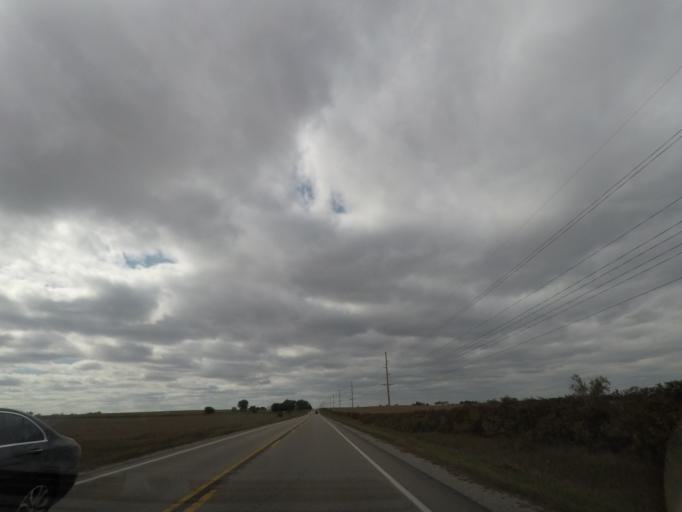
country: US
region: Iowa
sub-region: Story County
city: Huxley
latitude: 41.8778
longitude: -93.5415
